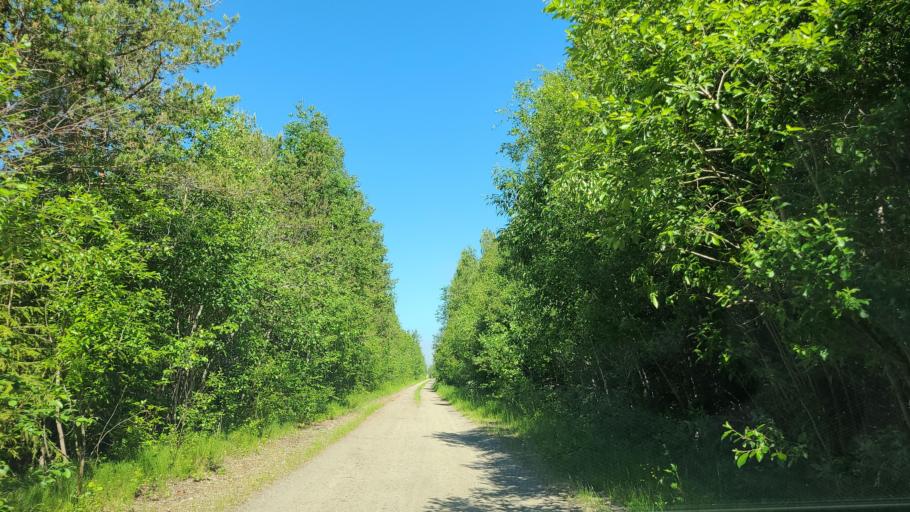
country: SE
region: Vaesternorrland
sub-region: OErnskoeldsviks Kommun
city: Husum
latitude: 63.4233
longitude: 19.2246
